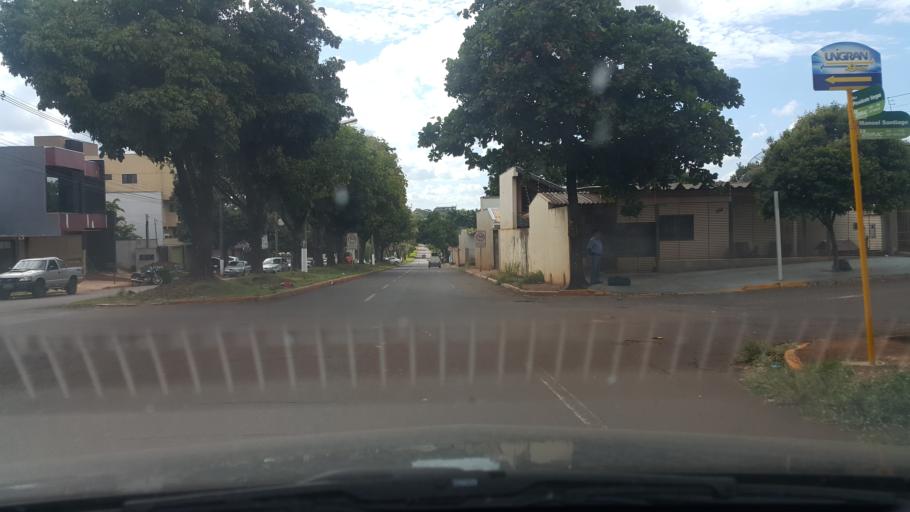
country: BR
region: Mato Grosso do Sul
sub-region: Dourados
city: Dourados
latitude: -22.2129
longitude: -54.8136
